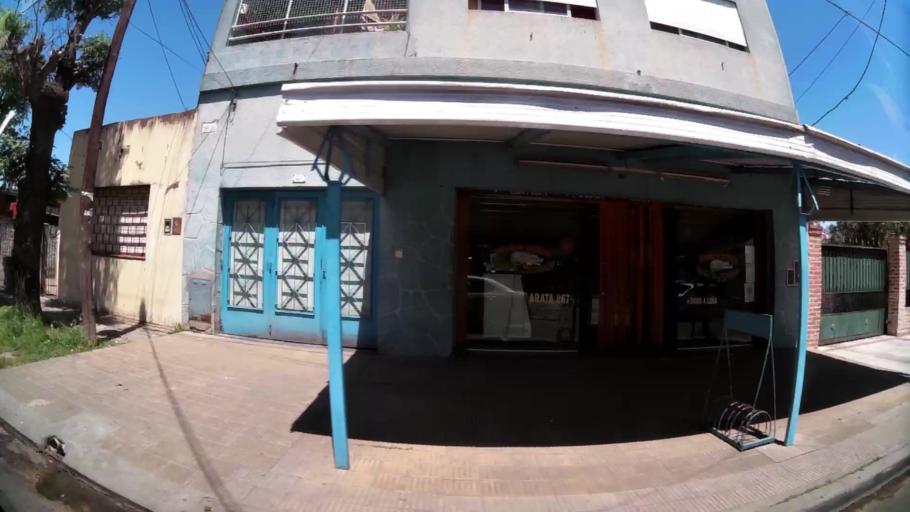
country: AR
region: Buenos Aires
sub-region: Partido de Tigre
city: Tigre
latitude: -34.4887
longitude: -58.6362
